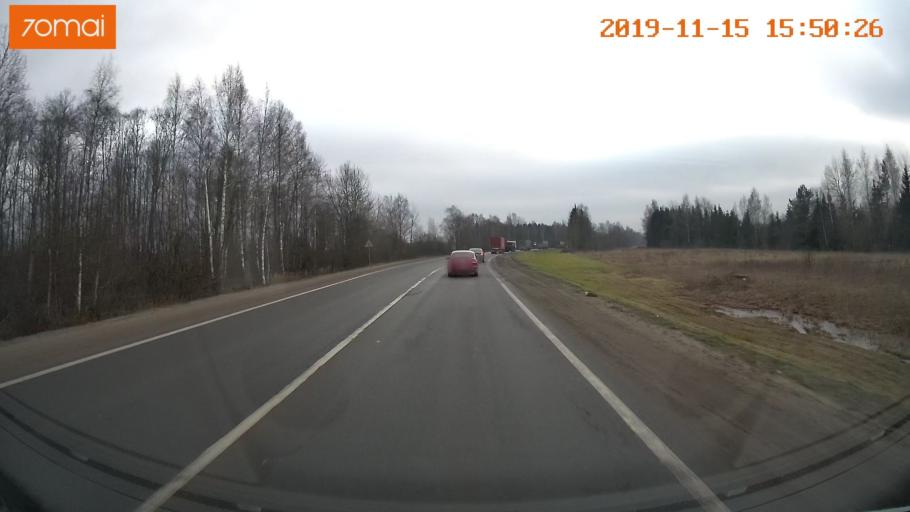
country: RU
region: Jaroslavl
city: Yaroslavl
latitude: 57.9055
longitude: 40.0133
